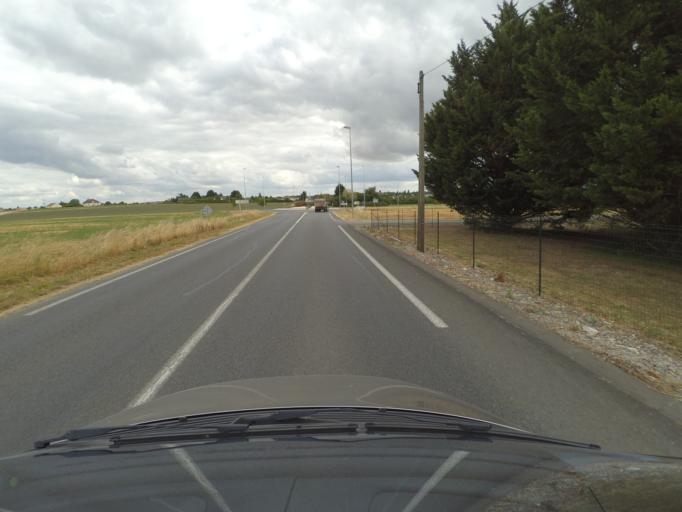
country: FR
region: Centre
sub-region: Departement d'Indre-et-Loire
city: Richelieu
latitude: 47.0108
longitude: 0.3038
